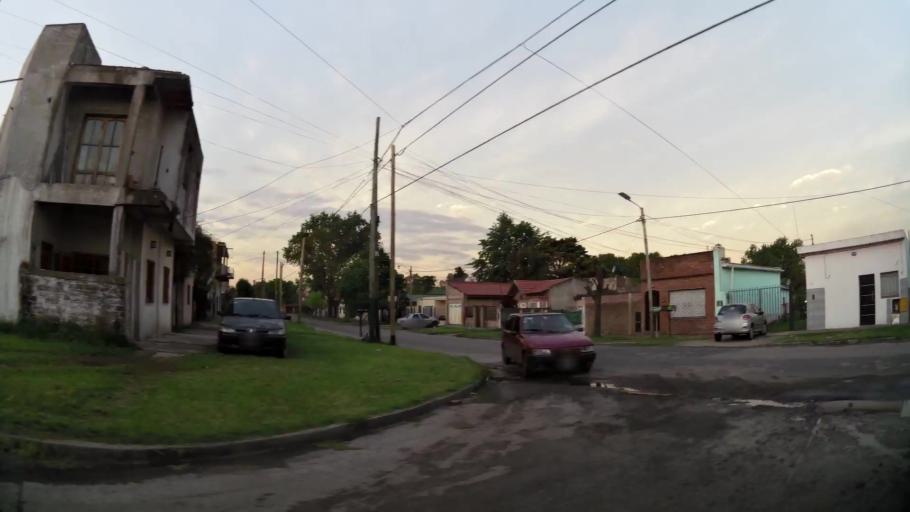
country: AR
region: Buenos Aires
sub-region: Partido de Lomas de Zamora
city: Lomas de Zamora
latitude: -34.7567
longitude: -58.3685
